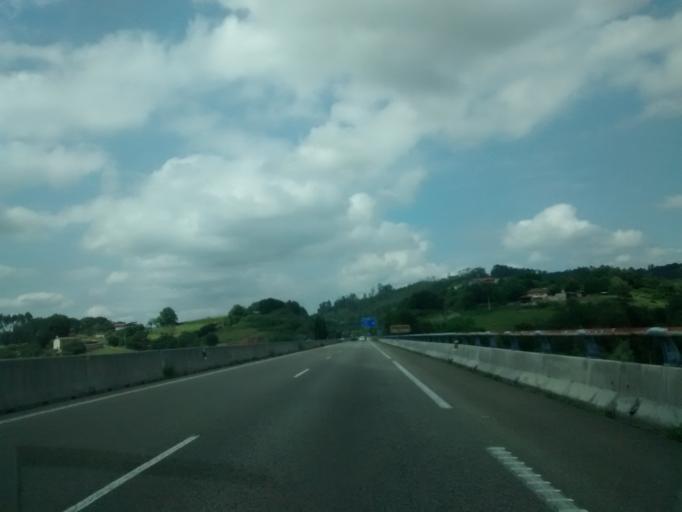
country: ES
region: Asturias
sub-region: Province of Asturias
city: Pola de Siero
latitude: 43.3633
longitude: -5.6830
